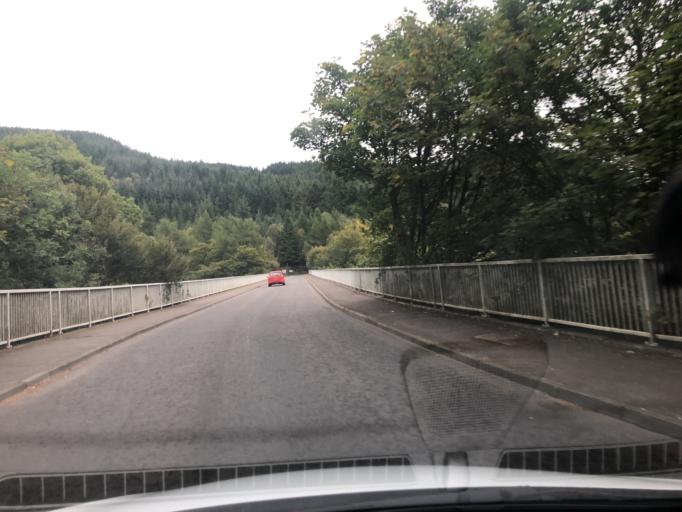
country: GB
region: Scotland
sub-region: Perth and Kinross
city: Pitlochry
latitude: 56.7279
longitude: -3.7774
